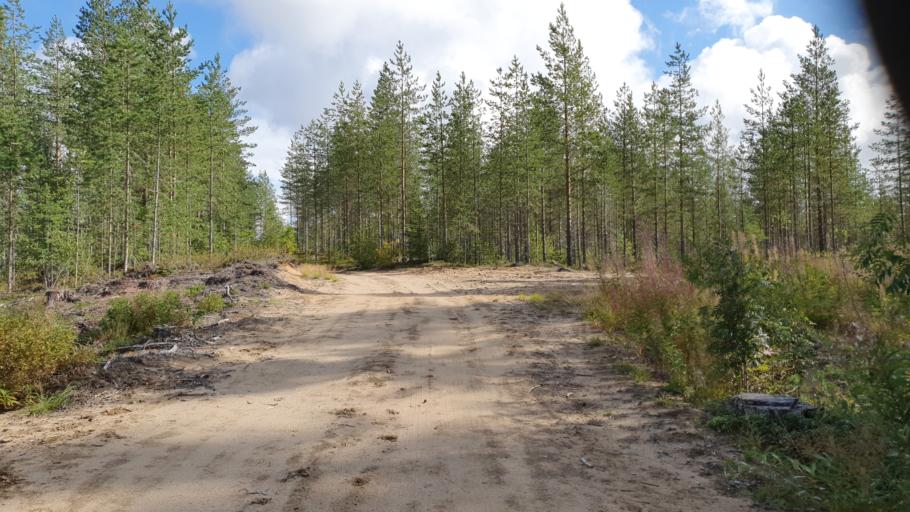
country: FI
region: Kainuu
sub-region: Kehys-Kainuu
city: Kuhmo
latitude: 64.1488
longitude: 29.3550
